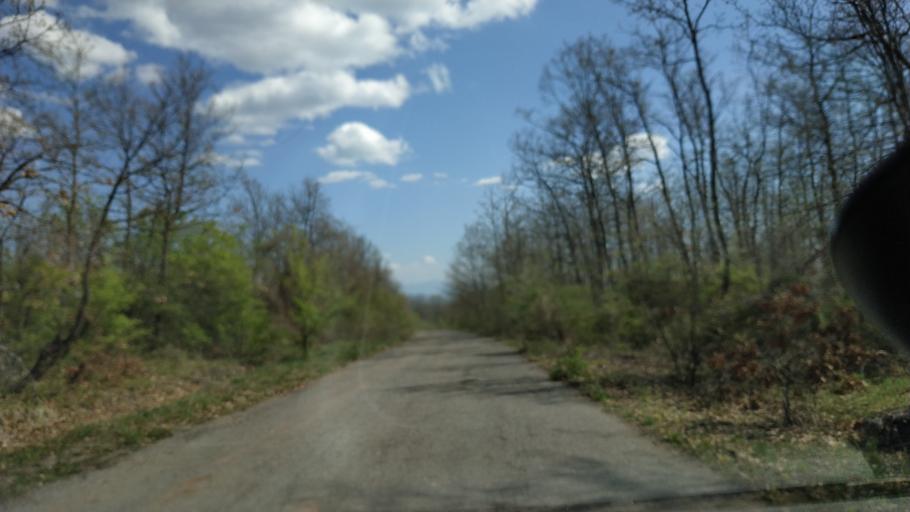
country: RS
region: Central Serbia
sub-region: Zajecarski Okrug
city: Soko Banja
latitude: 43.5443
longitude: 21.9015
